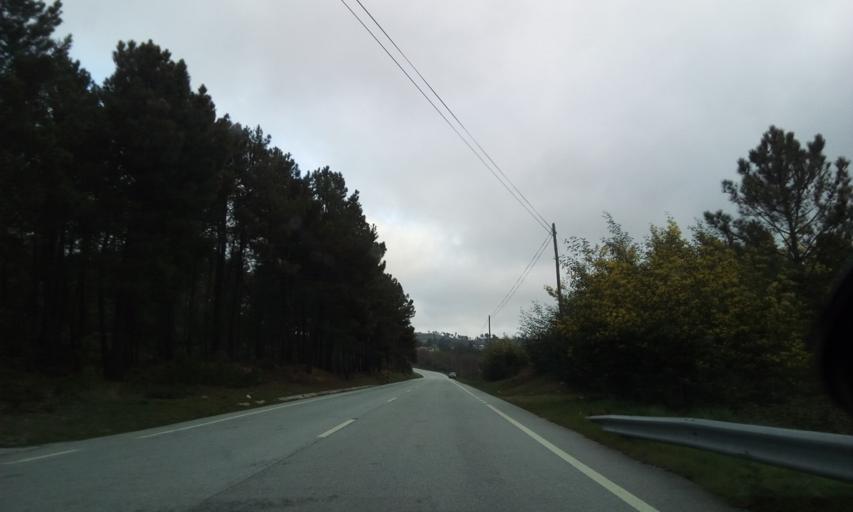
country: PT
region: Guarda
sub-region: Fornos de Algodres
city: Fornos de Algodres
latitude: 40.6472
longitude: -7.4908
